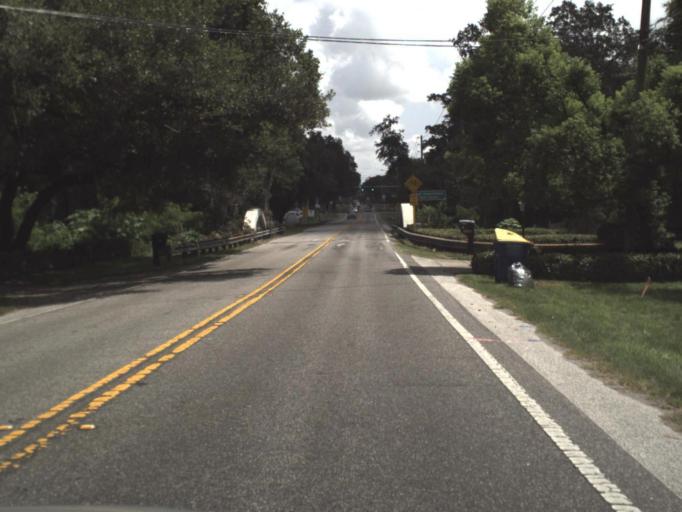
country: US
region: Florida
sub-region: Pinellas County
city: Safety Harbor
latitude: 27.9761
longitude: -82.7402
